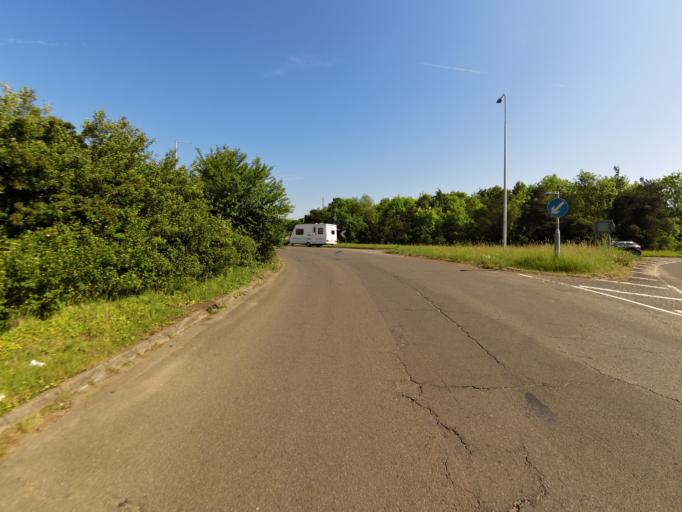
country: GB
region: England
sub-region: Suffolk
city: Bramford
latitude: 52.1026
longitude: 1.1065
